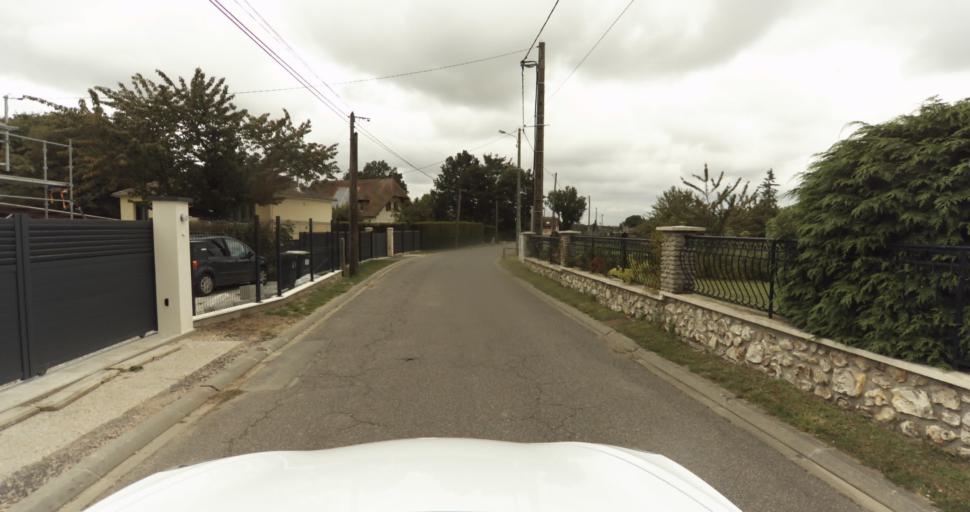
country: FR
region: Haute-Normandie
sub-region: Departement de l'Eure
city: Saint-Sebastien-de-Morsent
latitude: 49.0077
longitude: 1.0651
